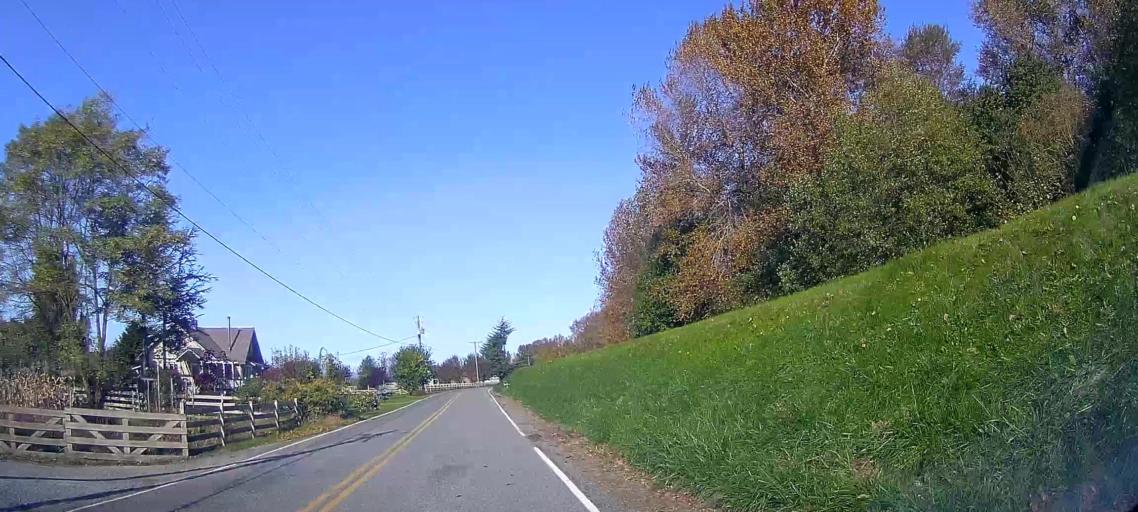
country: US
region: Washington
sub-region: Skagit County
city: Mount Vernon
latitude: 48.4029
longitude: -122.3683
